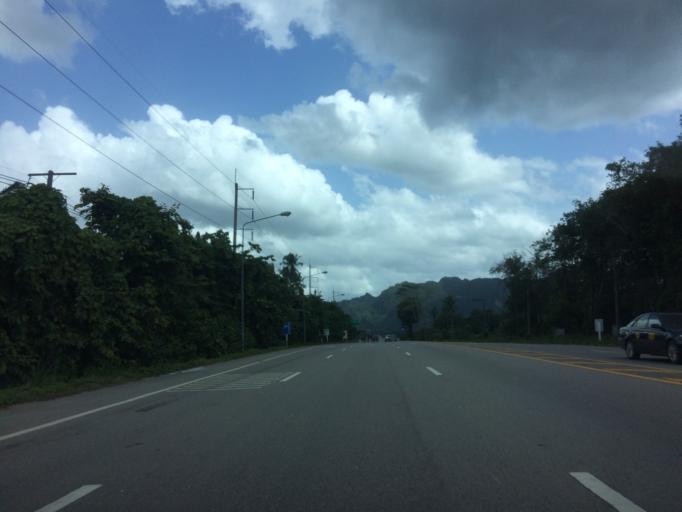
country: TH
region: Krabi
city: Ao Luek
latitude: 8.2324
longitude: 98.8086
